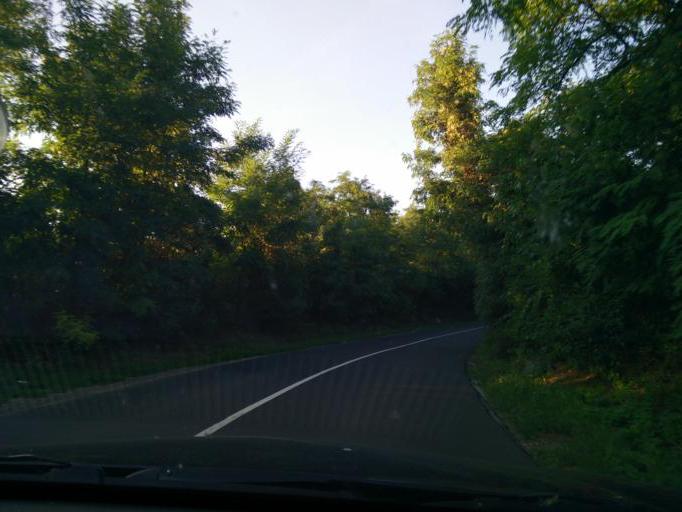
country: HU
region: Pest
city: Perbal
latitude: 47.6339
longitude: 18.7794
